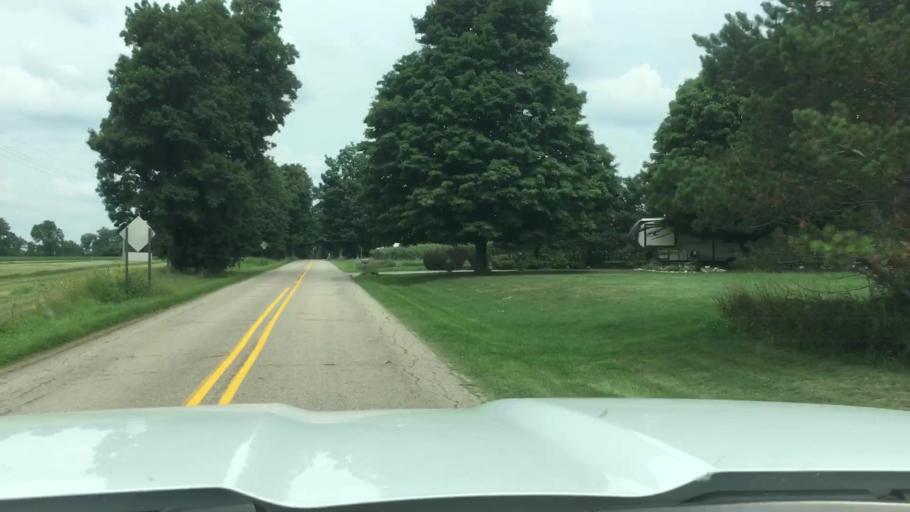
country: US
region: Michigan
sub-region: Ingham County
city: Webberville
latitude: 42.6941
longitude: -84.1905
